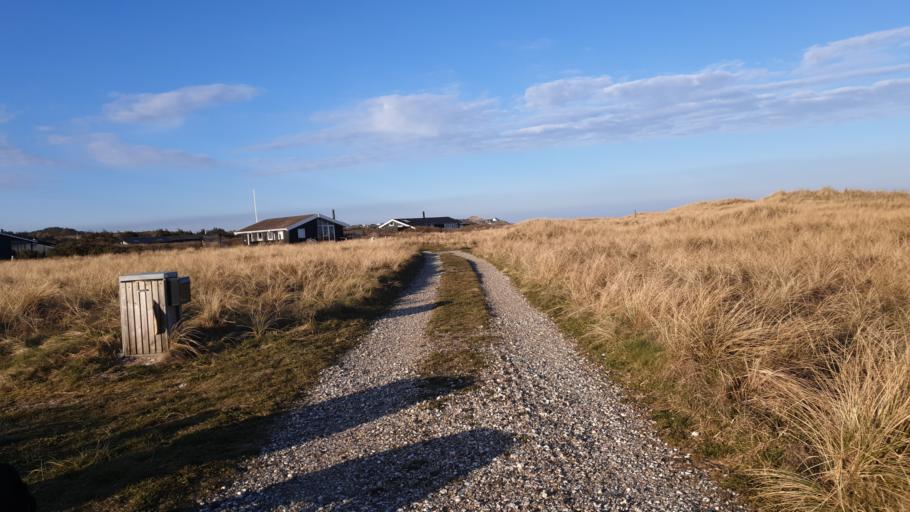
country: DK
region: North Denmark
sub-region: Hjorring Kommune
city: Hjorring
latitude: 57.4909
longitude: 9.8239
